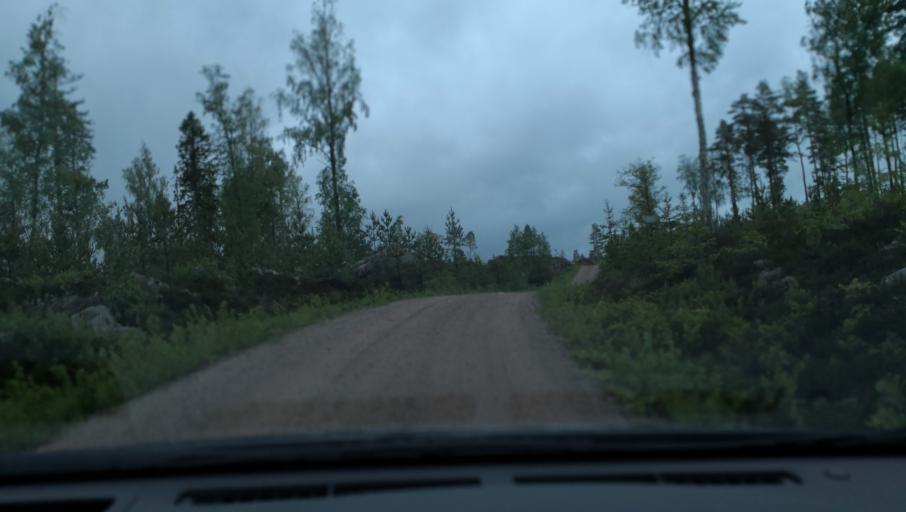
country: SE
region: Uppsala
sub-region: Enkopings Kommun
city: Orsundsbro
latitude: 59.9368
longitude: 17.3125
